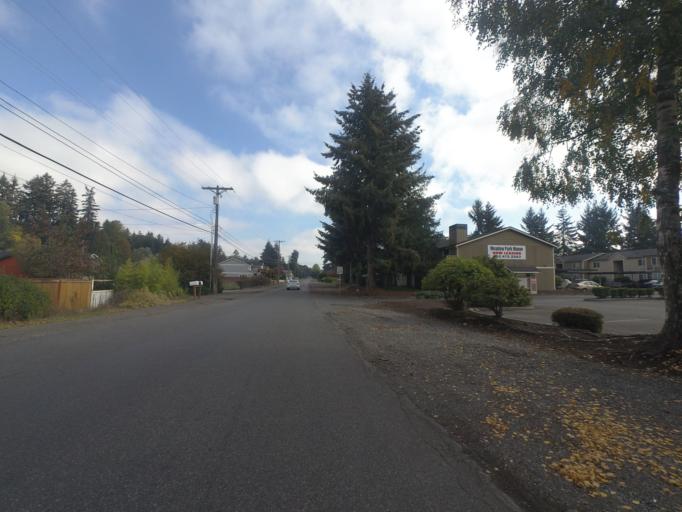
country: US
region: Washington
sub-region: Pierce County
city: Lakewood
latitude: 47.1993
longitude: -122.5084
